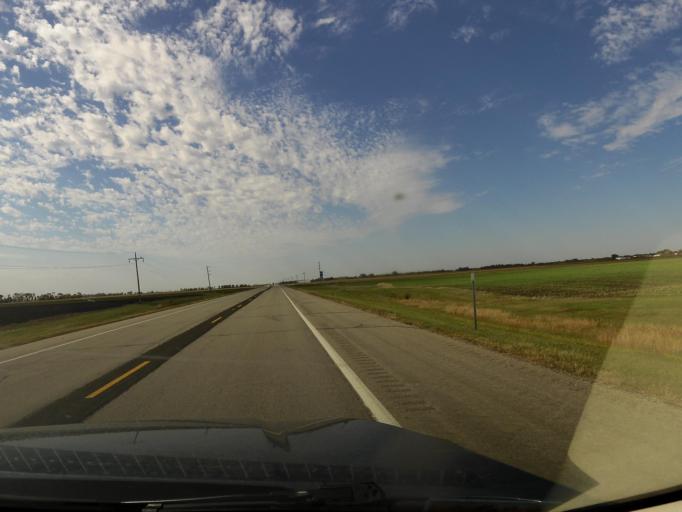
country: US
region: North Dakota
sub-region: Walsh County
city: Grafton
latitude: 48.4116
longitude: -97.2736
